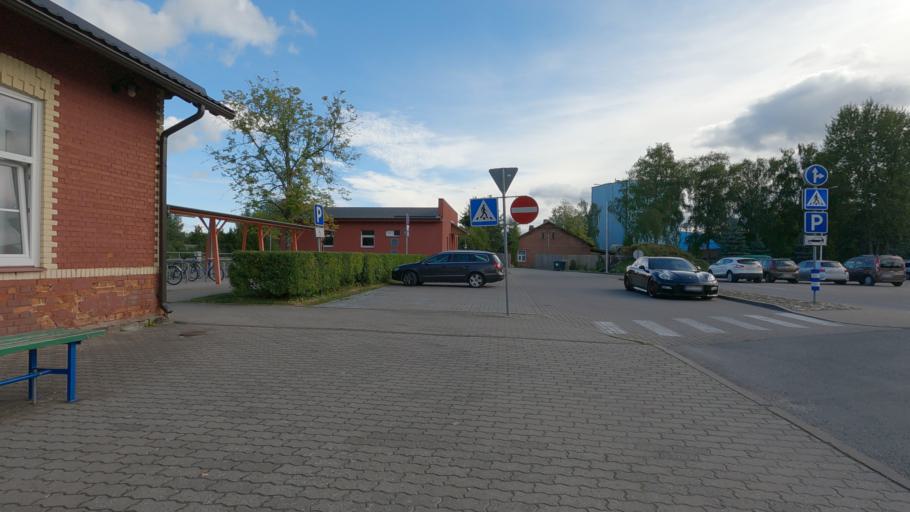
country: EE
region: Raplamaa
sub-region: Rapla vald
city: Rapla
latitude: 58.9934
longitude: 24.8323
